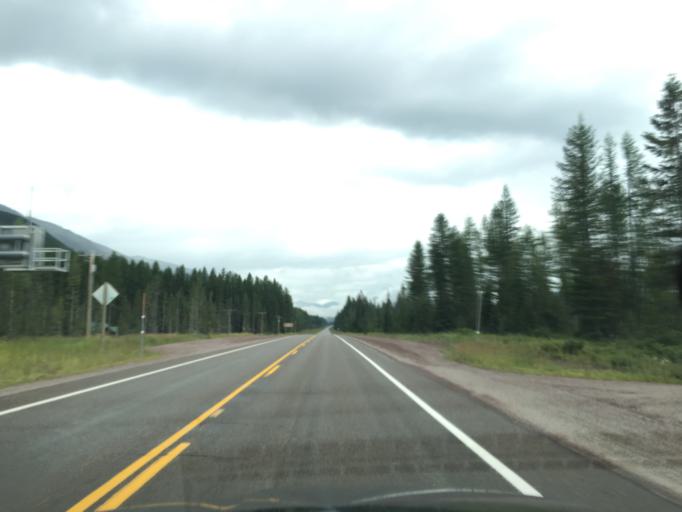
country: US
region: Montana
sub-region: Flathead County
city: Bigfork
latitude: 48.2855
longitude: -113.6074
